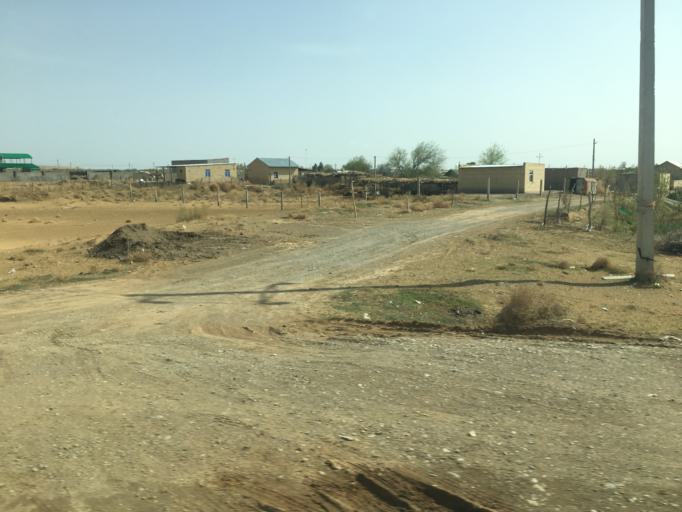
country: TM
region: Mary
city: Seydi
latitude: 39.4082
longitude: 62.9365
